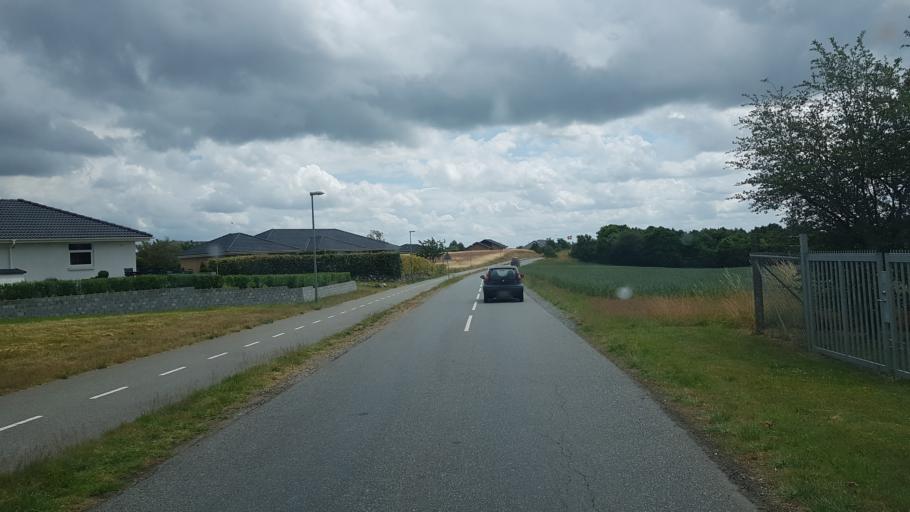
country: DK
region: South Denmark
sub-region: Kolding Kommune
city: Lunderskov
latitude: 55.4814
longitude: 9.2804
